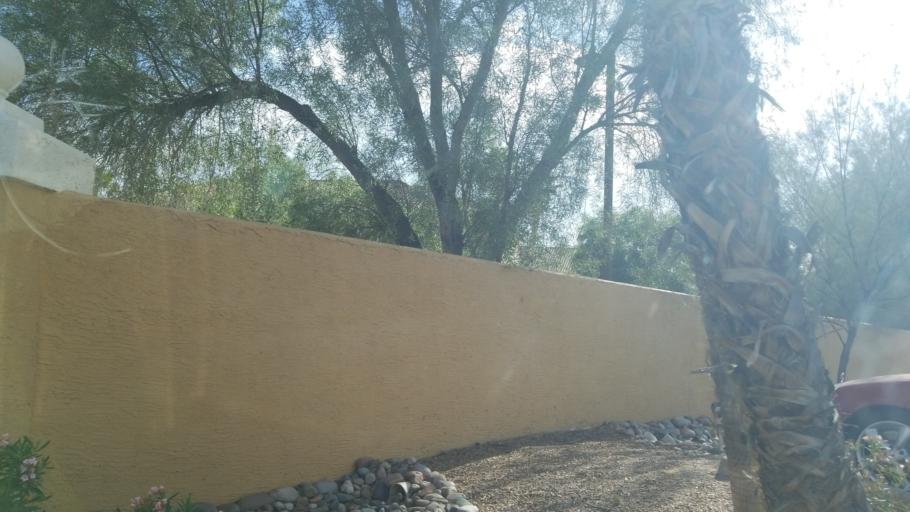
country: US
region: Arizona
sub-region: Maricopa County
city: Paradise Valley
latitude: 33.5842
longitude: -111.9327
